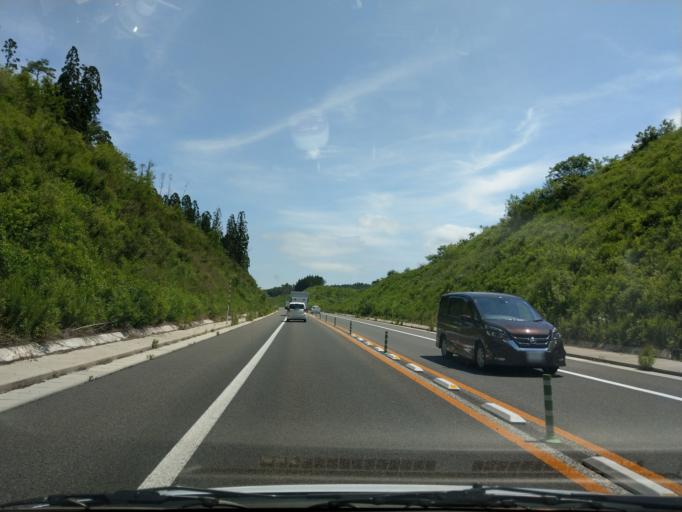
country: JP
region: Akita
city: Takanosu
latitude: 40.2090
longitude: 140.4114
